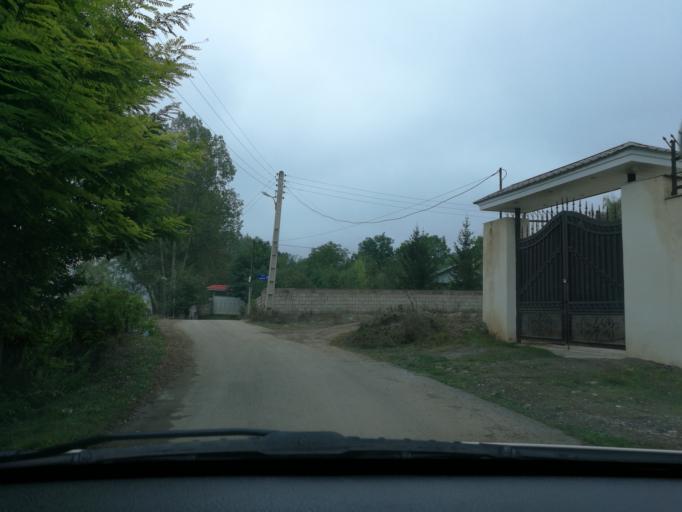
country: IR
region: Mazandaran
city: `Abbasabad
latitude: 36.5058
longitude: 51.1936
